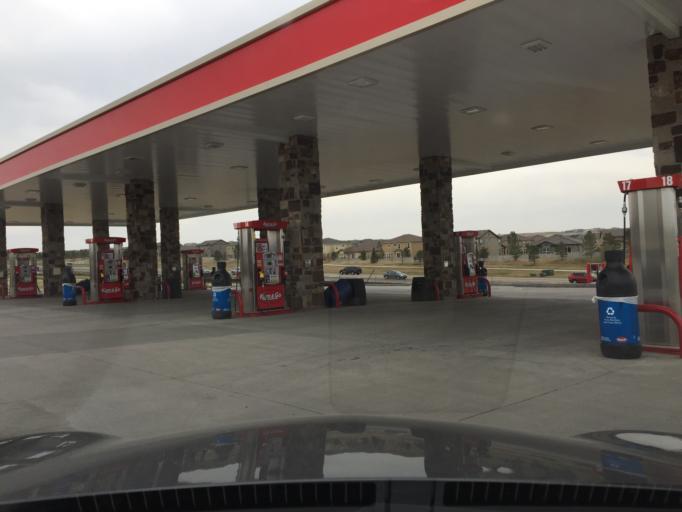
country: US
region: Colorado
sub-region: Boulder County
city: Erie
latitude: 40.0010
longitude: -105.0365
